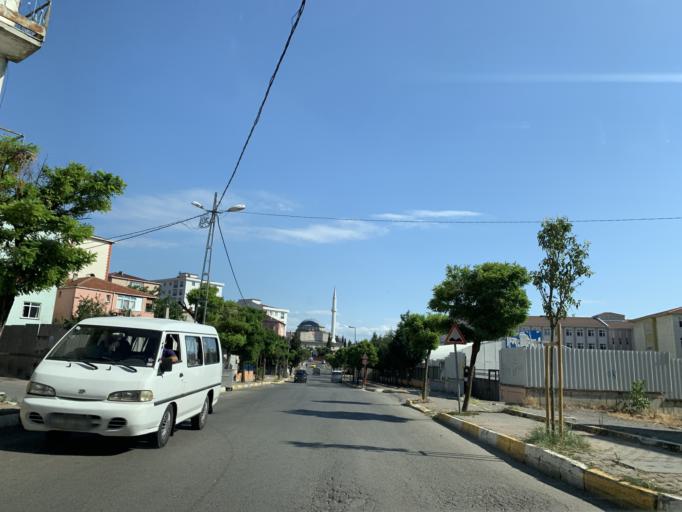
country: TR
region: Istanbul
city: Pendik
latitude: 40.8830
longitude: 29.2798
